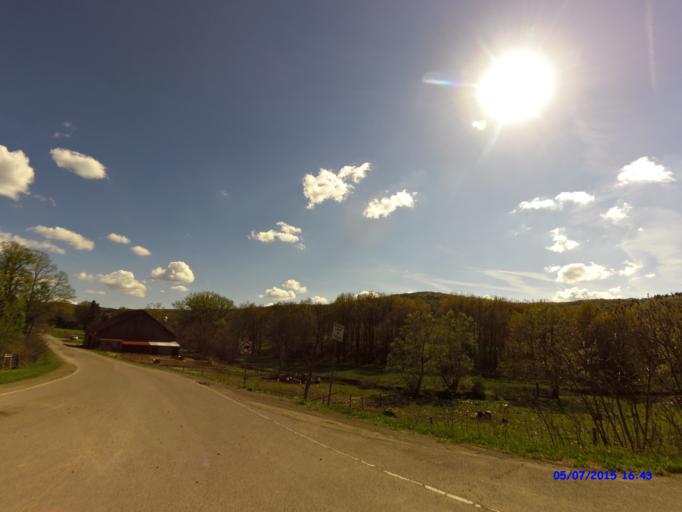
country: US
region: New York
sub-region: Cattaraugus County
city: Little Valley
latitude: 42.3045
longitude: -78.7163
